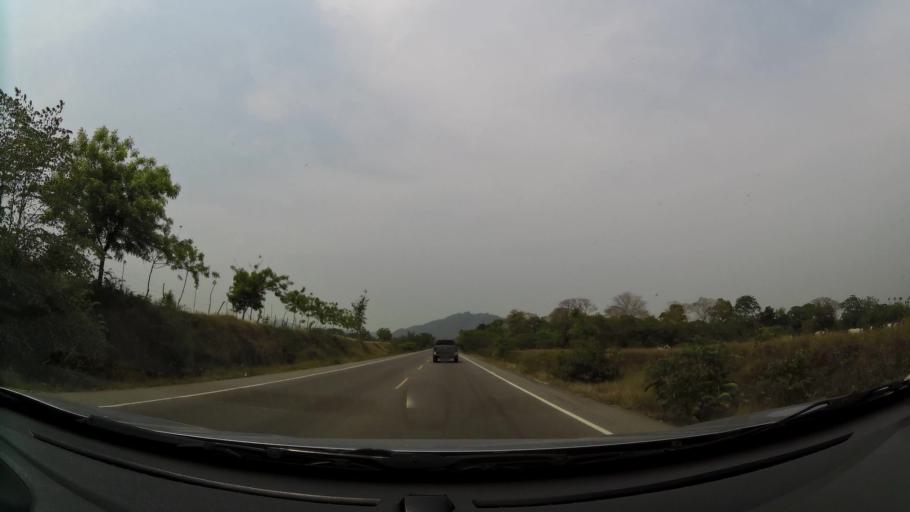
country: HN
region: Cortes
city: Potrerillos
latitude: 15.2448
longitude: -87.9557
